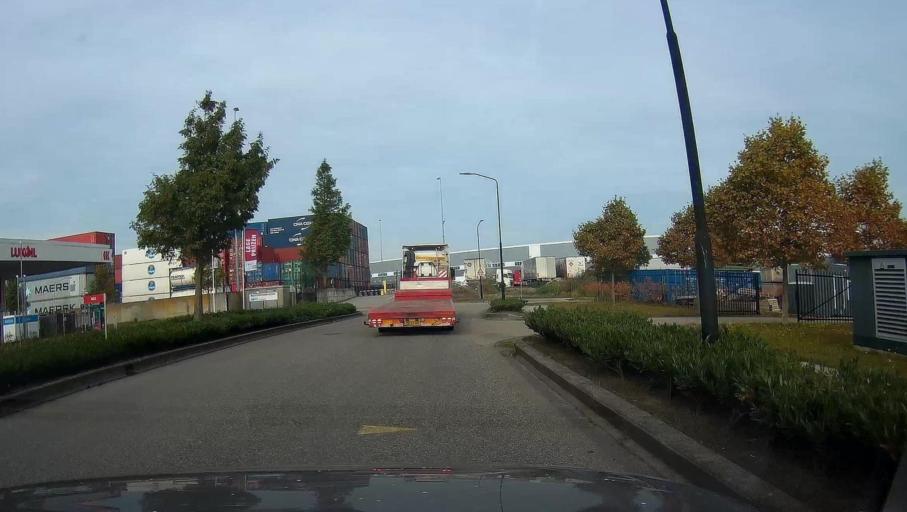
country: NL
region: South Holland
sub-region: Gemeente Papendrecht
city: Papendrecht
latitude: 51.8463
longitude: 4.6717
